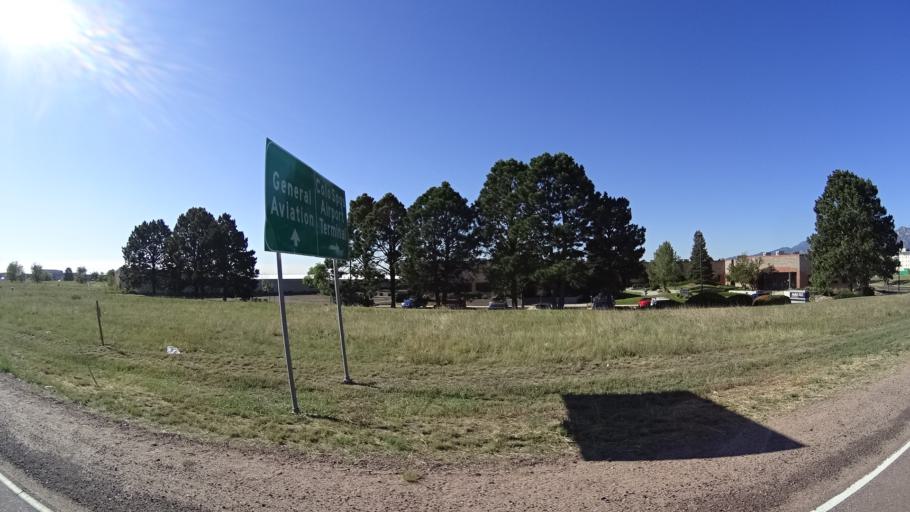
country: US
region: Colorado
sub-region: El Paso County
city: Stratmoor
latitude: 38.8061
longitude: -104.7331
